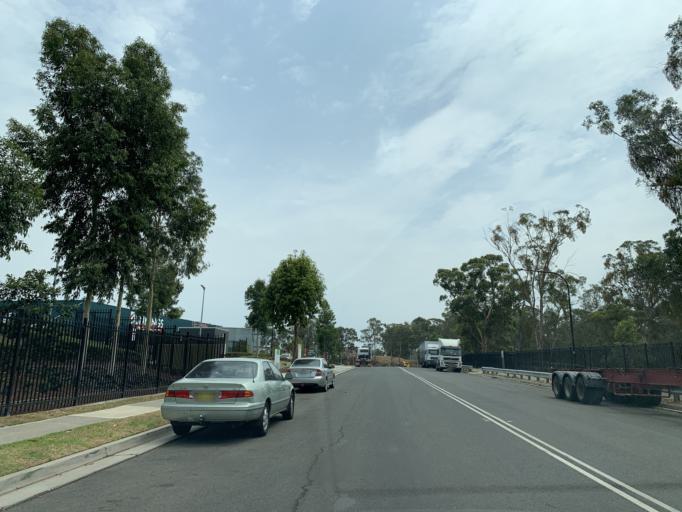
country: AU
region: New South Wales
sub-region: Blacktown
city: Blacktown
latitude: -33.8009
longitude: 150.8998
